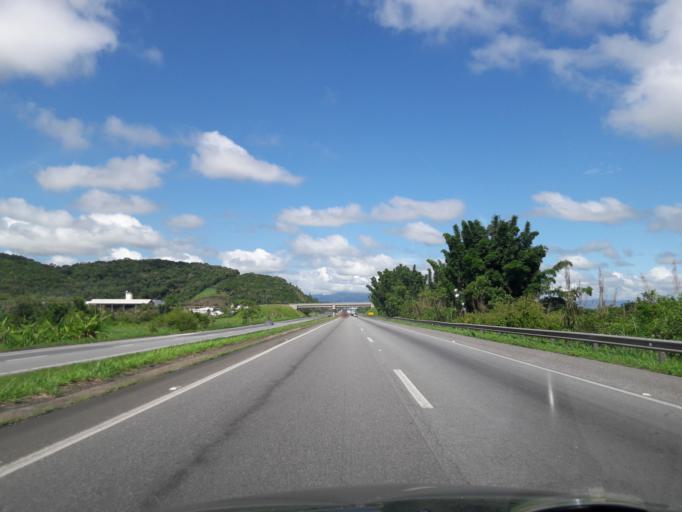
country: BR
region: Sao Paulo
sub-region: Jacupiranga
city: Jacupiranga
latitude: -24.6842
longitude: -47.9870
